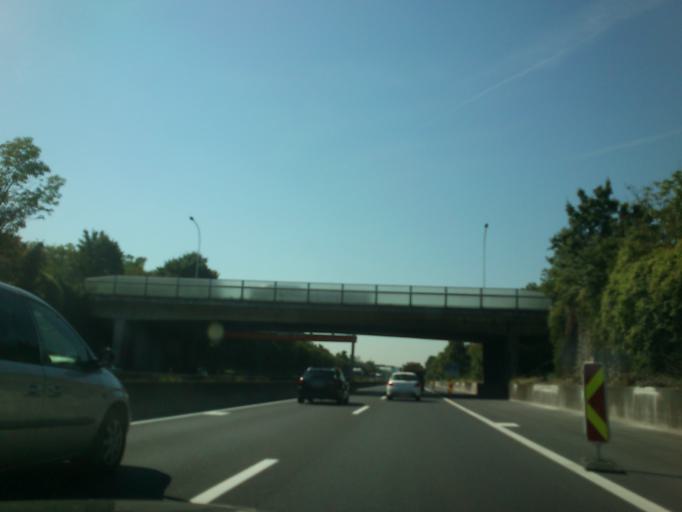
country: AT
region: Upper Austria
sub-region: Politischer Bezirk Linz-Land
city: Ansfelden
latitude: 48.2527
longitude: 14.2971
